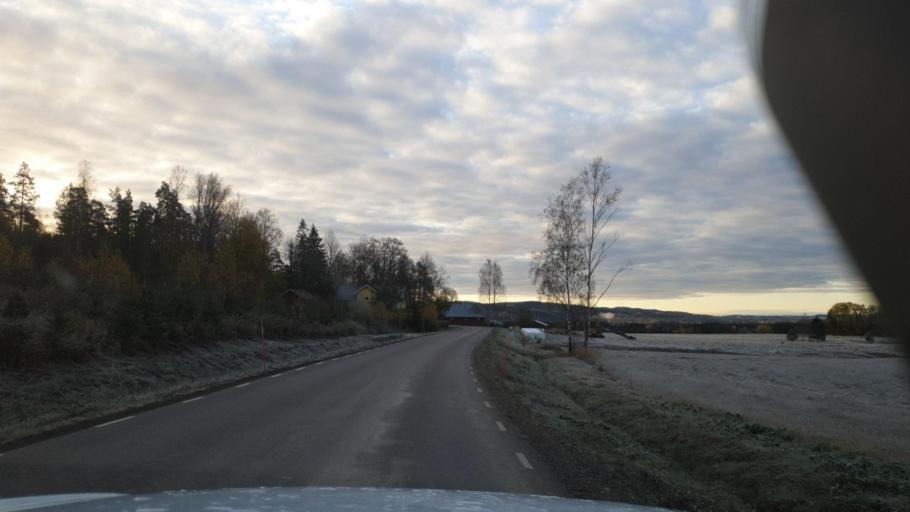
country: SE
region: Vaermland
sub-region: Eda Kommun
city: Charlottenberg
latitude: 59.7510
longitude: 12.1596
